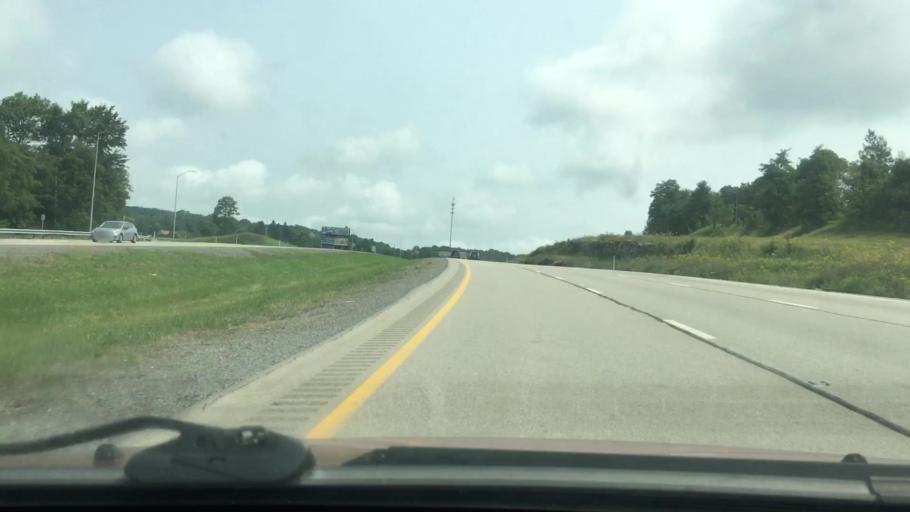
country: US
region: West Virginia
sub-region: Preston County
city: Terra Alta
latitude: 39.6602
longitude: -79.4951
